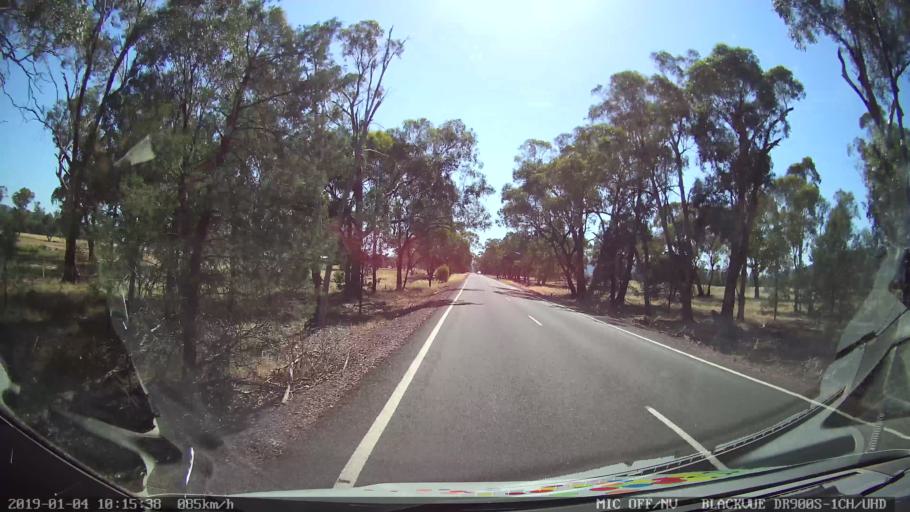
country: AU
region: New South Wales
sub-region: Cabonne
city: Canowindra
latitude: -33.3867
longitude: 148.4244
